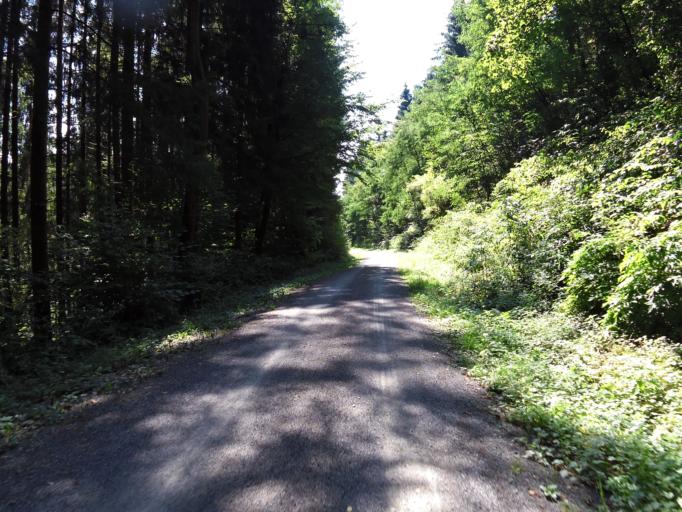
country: DE
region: Baden-Wuerttemberg
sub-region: Karlsruhe Region
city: Mosbach
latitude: 49.3798
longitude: 9.1524
